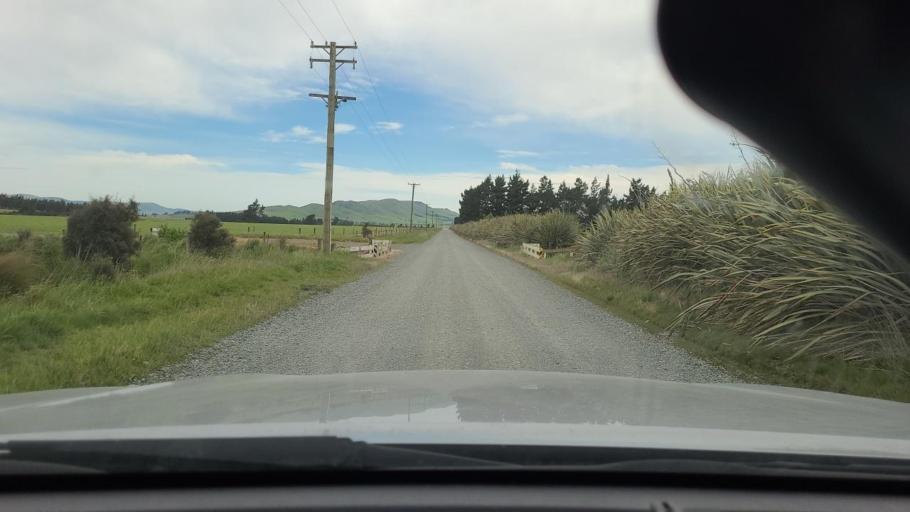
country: NZ
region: Southland
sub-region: Southland District
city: Winton
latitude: -45.6817
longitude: 168.1843
